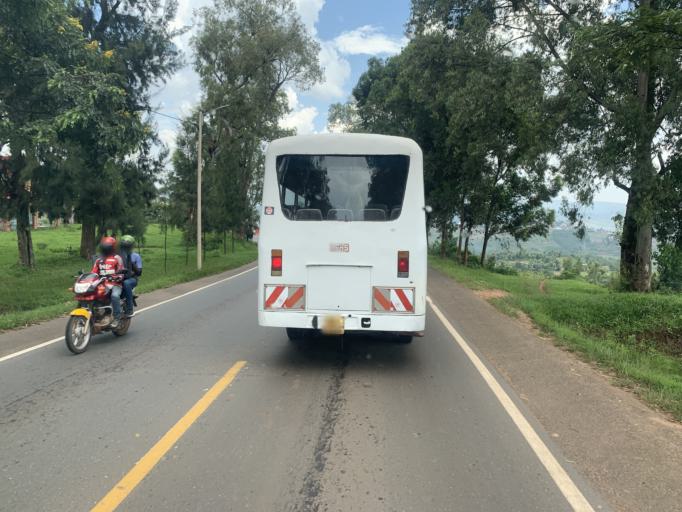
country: RW
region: Kigali
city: Kigali
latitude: -1.9943
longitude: 29.9165
